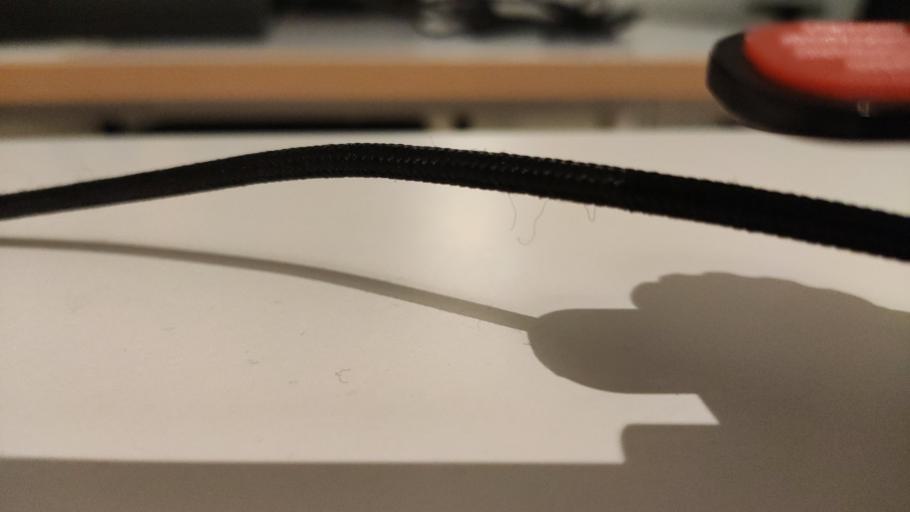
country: RU
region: Moskovskaya
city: Novosin'kovo
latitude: 56.3949
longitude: 37.2791
